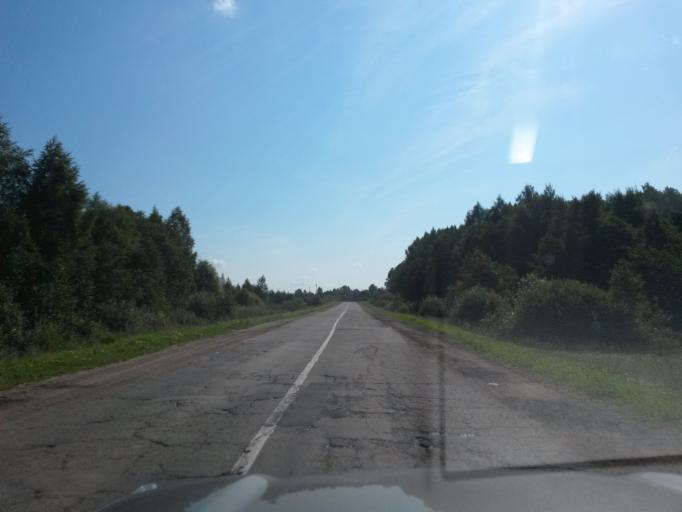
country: RU
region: Jaroslavl
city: Gavrilov-Yam
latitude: 57.3061
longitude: 39.9794
